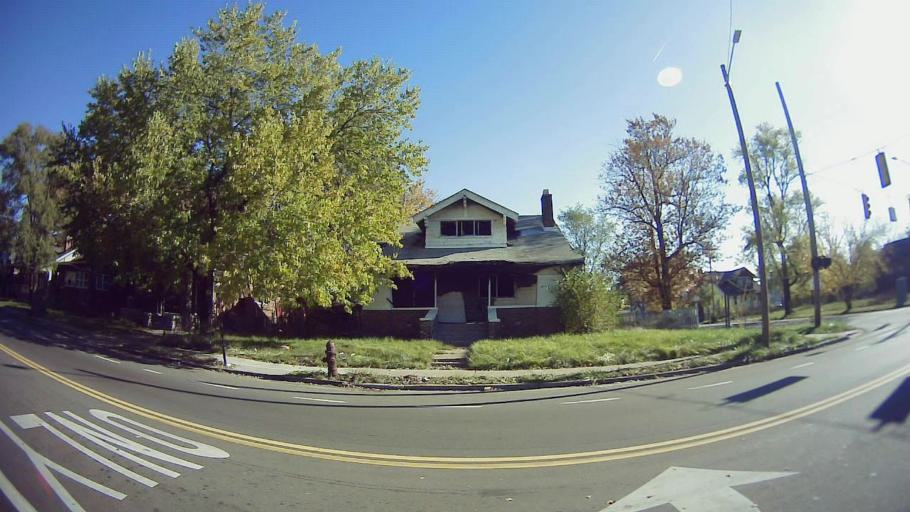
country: US
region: Michigan
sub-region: Wayne County
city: Dearborn
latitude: 42.3814
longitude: -83.1589
